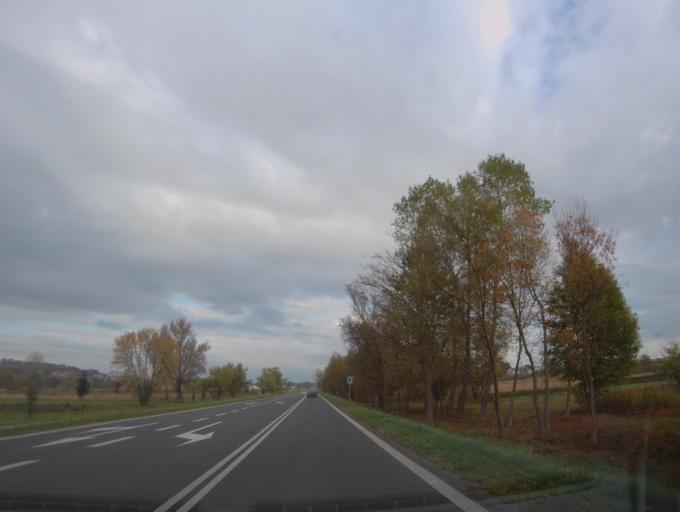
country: PL
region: Lublin Voivodeship
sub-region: Powiat bilgorajski
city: Goraj
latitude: 50.7136
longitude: 22.6780
